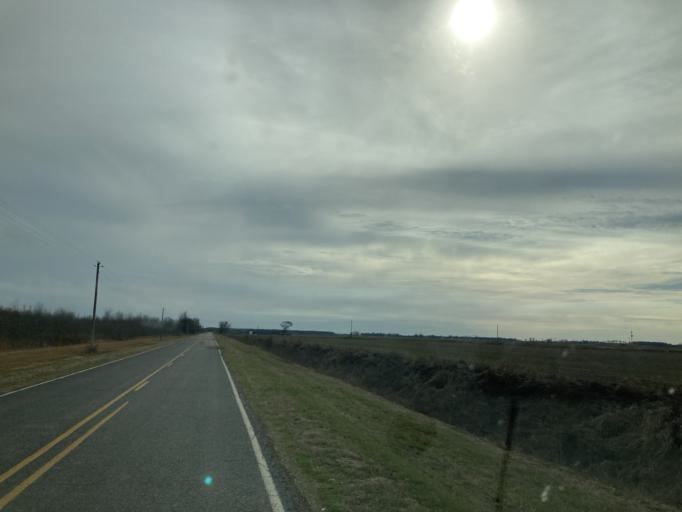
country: US
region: Mississippi
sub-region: Humphreys County
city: Belzoni
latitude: 33.1669
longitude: -90.5723
